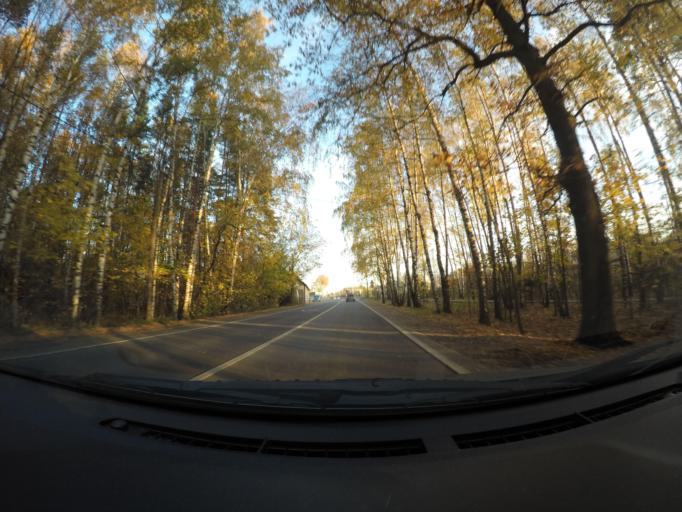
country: RU
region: Moskovskaya
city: Firsanovka
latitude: 55.9607
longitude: 37.2522
